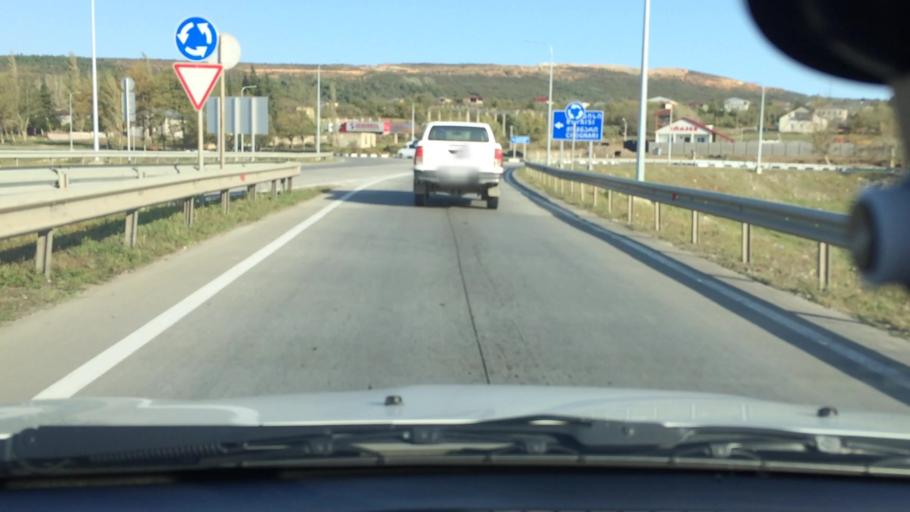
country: GE
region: Imereti
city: Kutaisi
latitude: 42.2126
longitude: 42.8194
